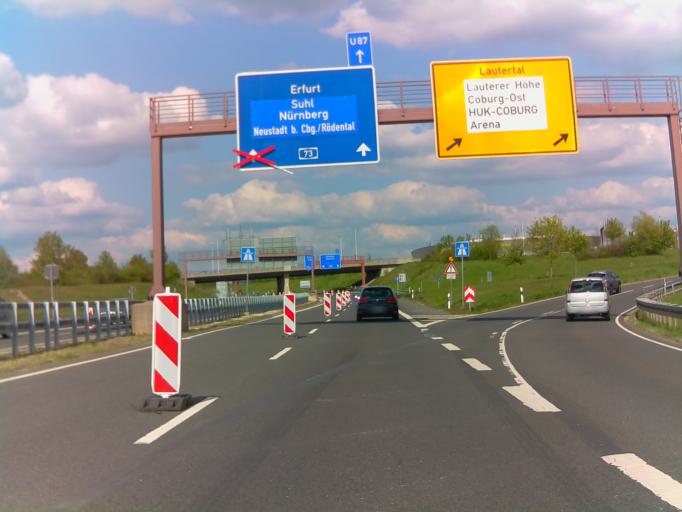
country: DE
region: Bavaria
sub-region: Upper Franconia
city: Coburg
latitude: 50.2859
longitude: 10.9748
